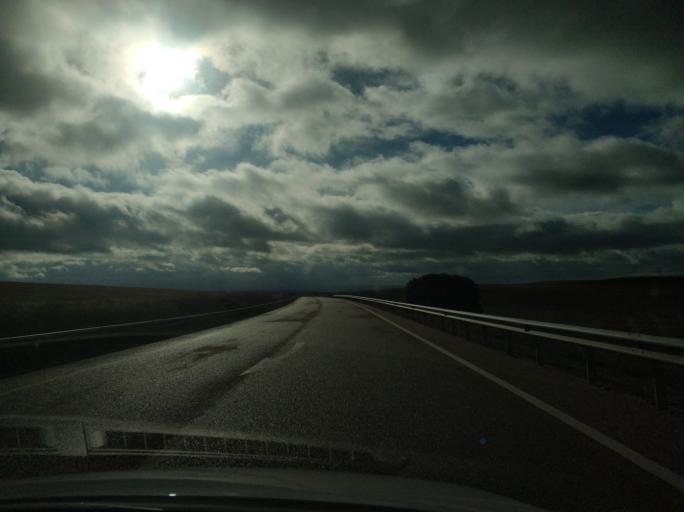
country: ES
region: Castille and Leon
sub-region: Provincia de Soria
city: Fuentecambron
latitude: 41.4570
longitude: -3.3357
